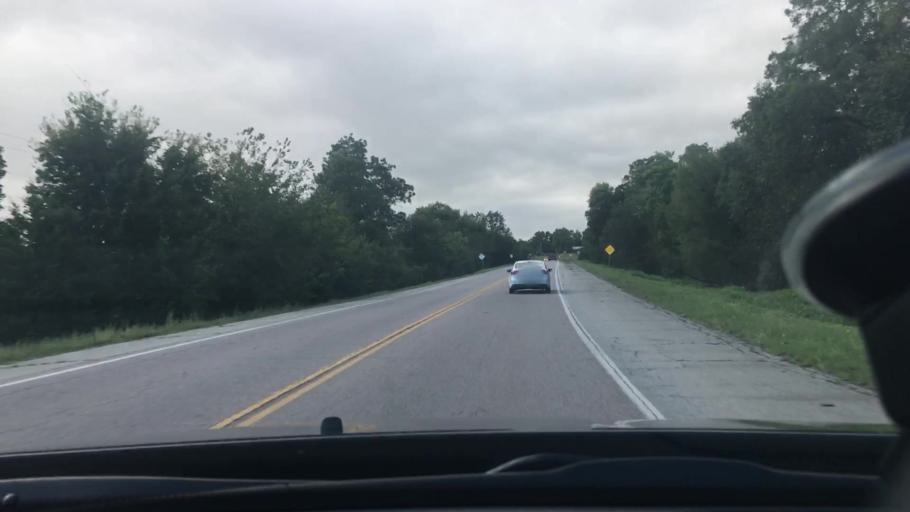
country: US
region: Oklahoma
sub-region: Coal County
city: Coalgate
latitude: 34.5474
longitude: -96.2303
